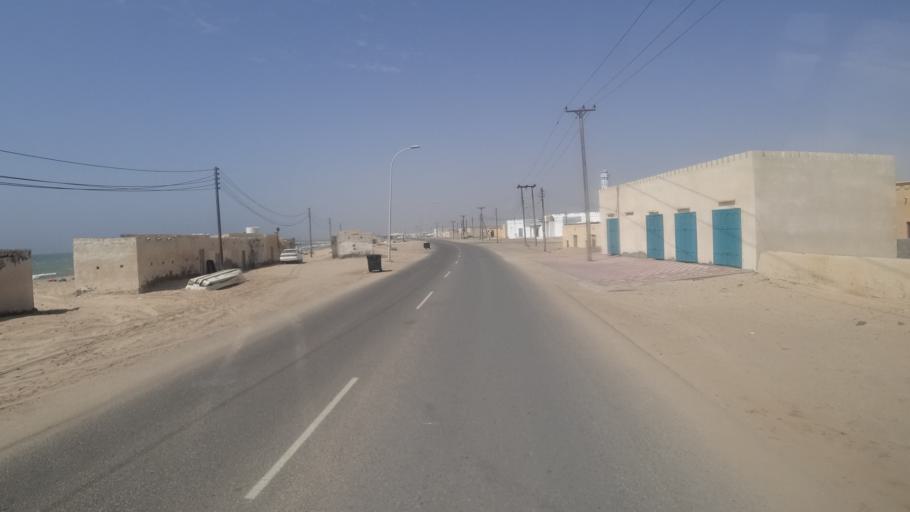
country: OM
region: Ash Sharqiyah
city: Sur
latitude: 22.1176
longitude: 59.7149
